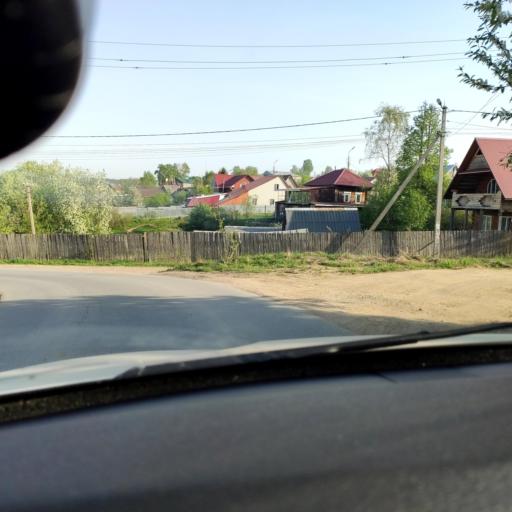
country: RU
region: Perm
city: Polazna
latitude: 58.2992
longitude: 56.4088
